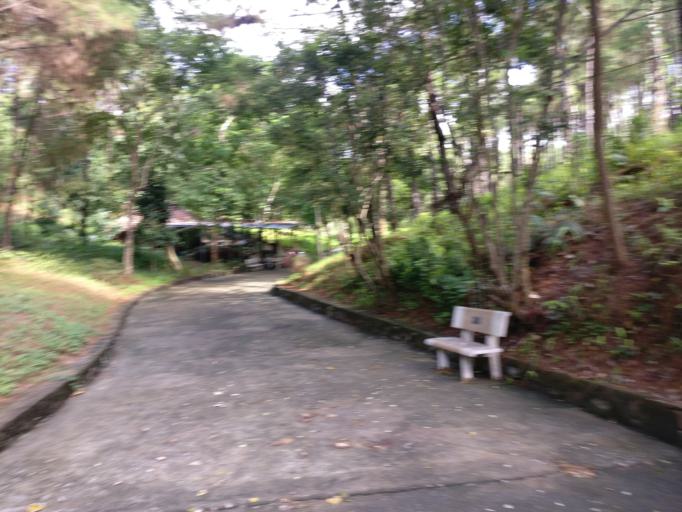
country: VN
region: Thua Thien-Hue
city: Hue
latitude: 16.4208
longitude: 107.6065
